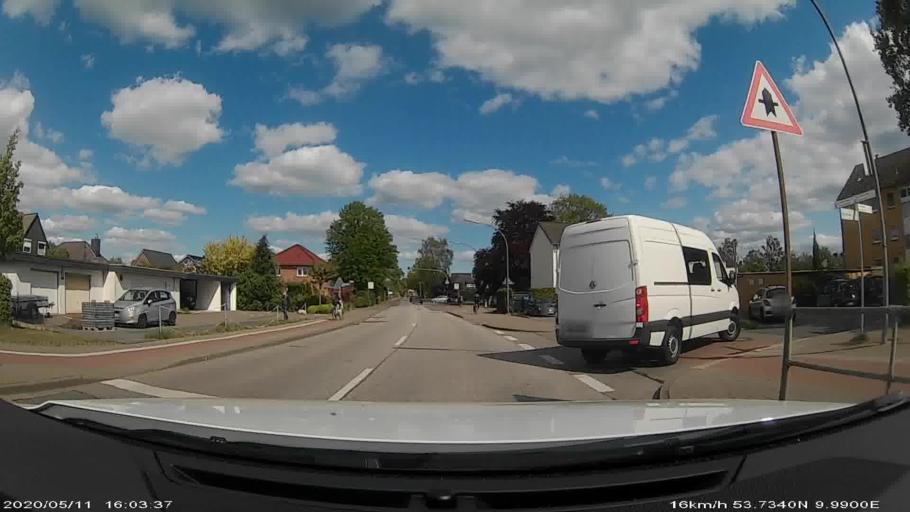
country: DE
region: Schleswig-Holstein
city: Norderstedt
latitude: 53.7357
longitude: 9.9965
